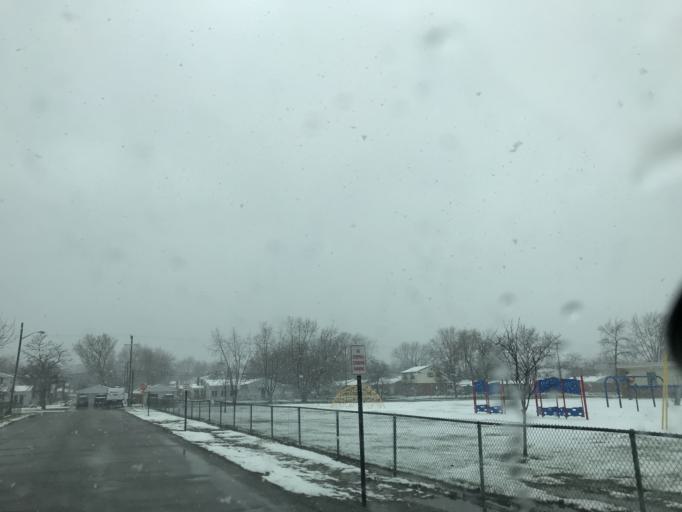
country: US
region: Michigan
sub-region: Wayne County
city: Taylor
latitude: 42.2309
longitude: -83.2482
